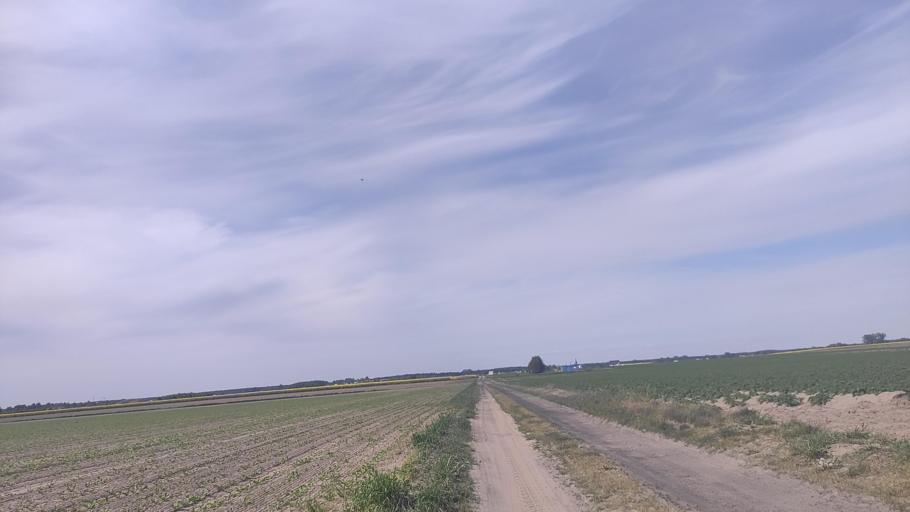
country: PL
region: Greater Poland Voivodeship
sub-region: Powiat poznanski
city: Swarzedz
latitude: 52.4148
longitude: 17.1093
